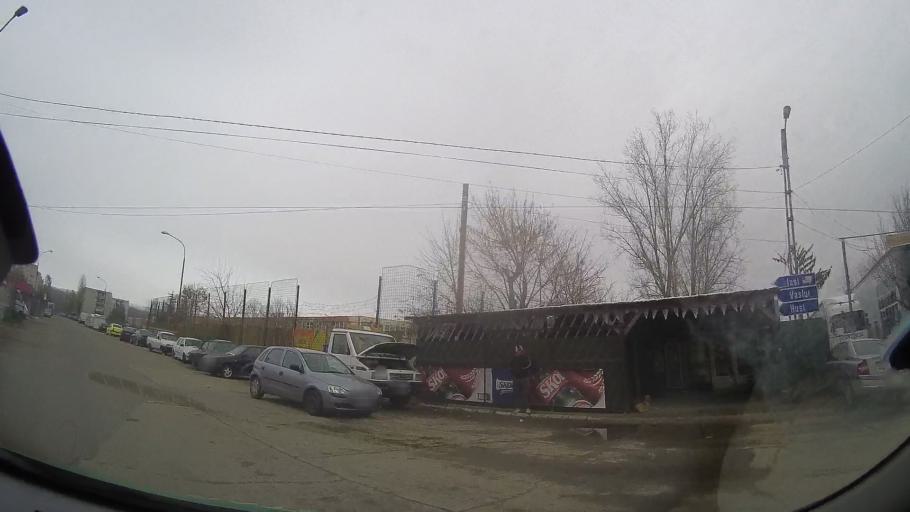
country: RO
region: Vaslui
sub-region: Municipiul Barlad
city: Barlad
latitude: 46.2374
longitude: 27.6791
